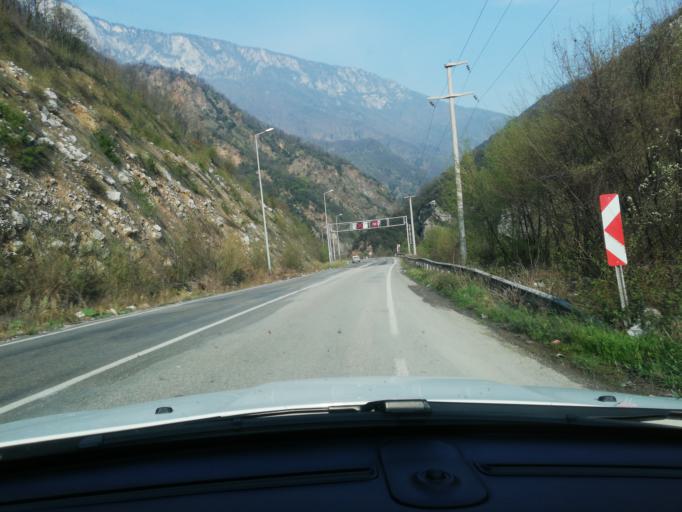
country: TR
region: Karabuk
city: Yenice
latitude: 41.1577
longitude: 32.4649
